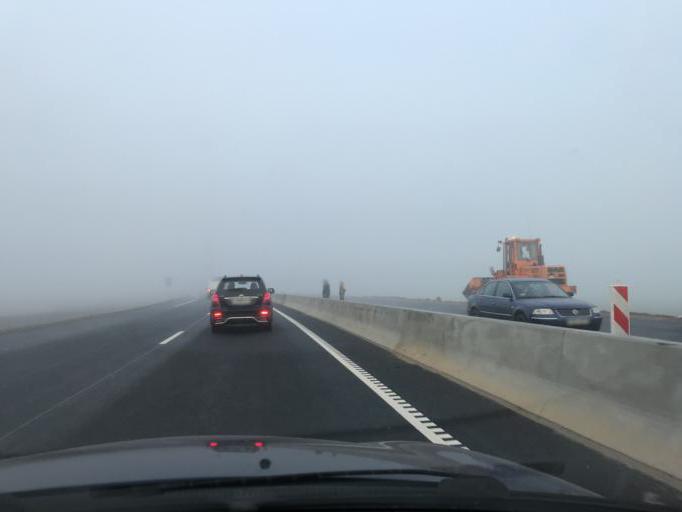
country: BY
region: Minsk
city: Valozhyn
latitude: 54.0657
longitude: 26.5202
